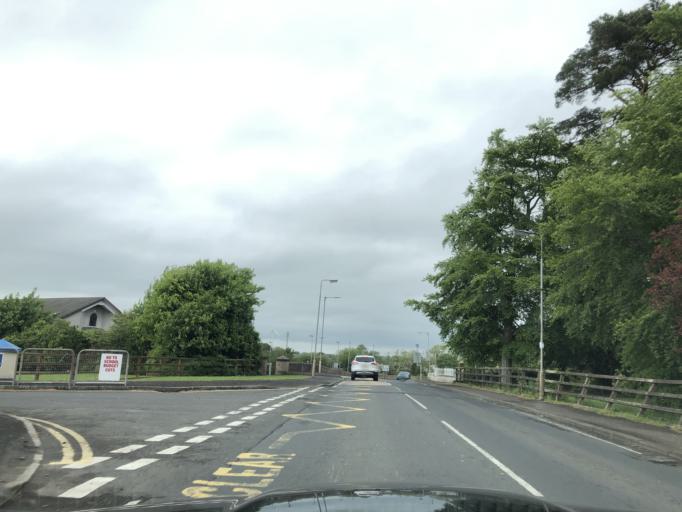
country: GB
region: Northern Ireland
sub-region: Antrim Borough
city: Templepatrick
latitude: 54.6137
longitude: -6.1206
